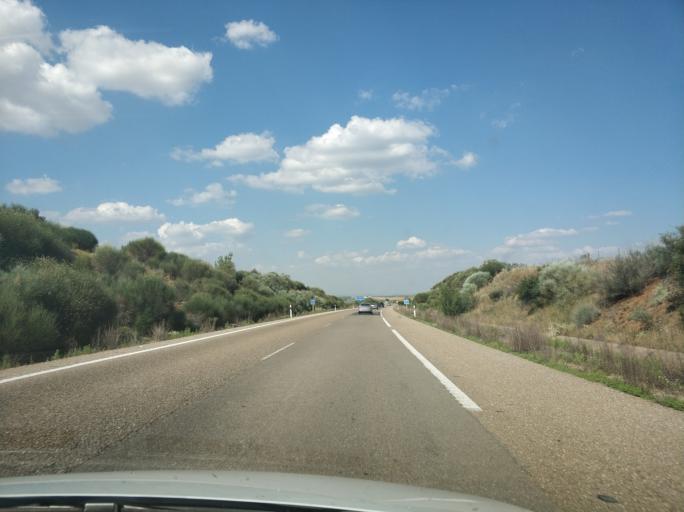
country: ES
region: Castille and Leon
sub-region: Provincia de Zamora
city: San Cristobal de Entrevinas
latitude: 42.0603
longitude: -5.6720
